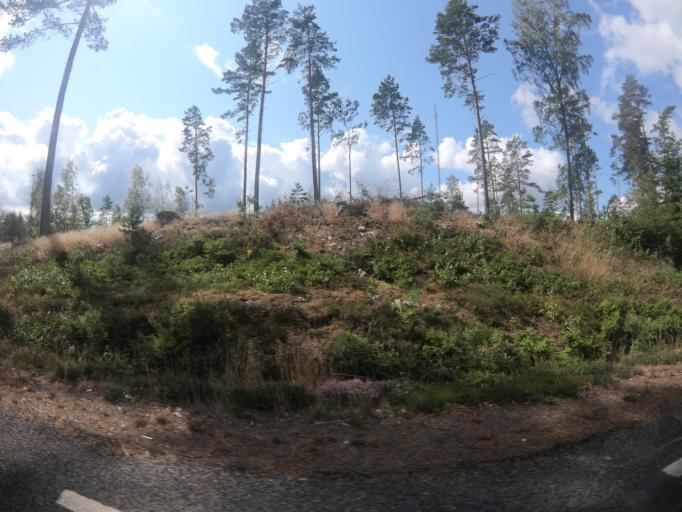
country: SE
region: Kronoberg
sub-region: Vaxjo Kommun
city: Braas
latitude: 57.0602
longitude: 15.0352
